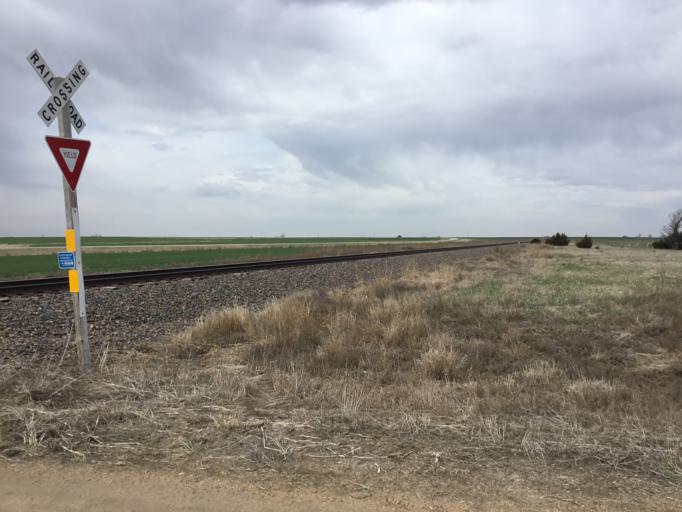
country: US
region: Kansas
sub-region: Russell County
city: Russell
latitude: 38.8852
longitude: -98.9561
